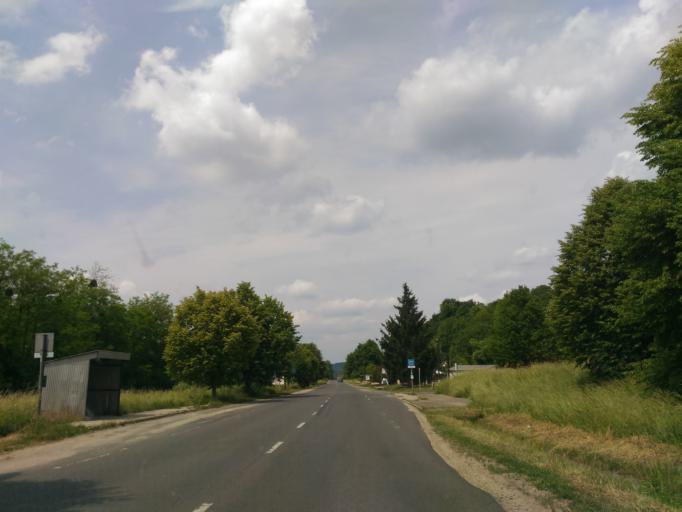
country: HU
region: Baranya
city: Komlo
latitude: 46.2010
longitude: 18.2514
